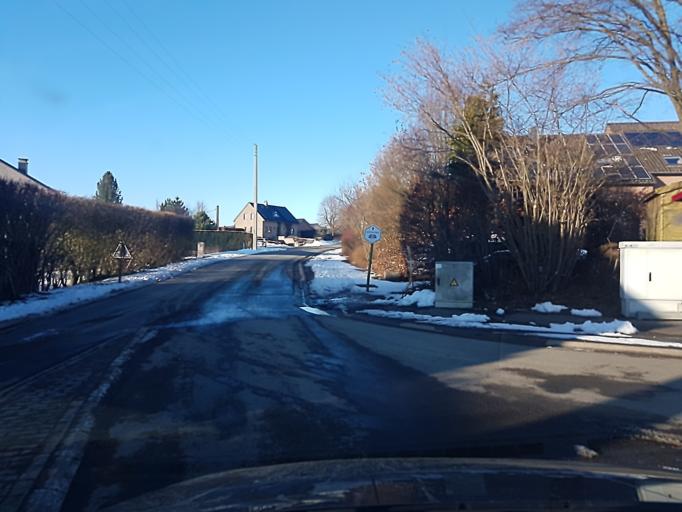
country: BE
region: Wallonia
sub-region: Province de Liege
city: Jalhay
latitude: 50.5518
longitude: 5.9665
